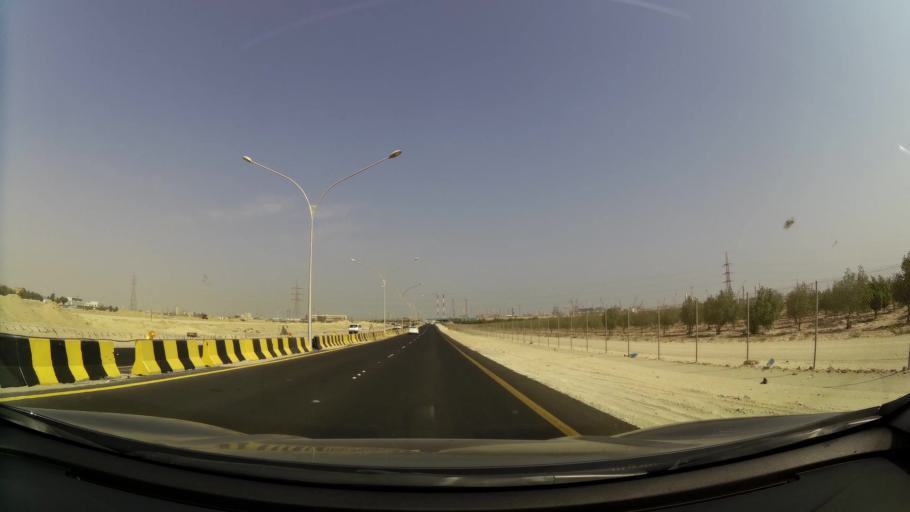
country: KW
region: Al Ahmadi
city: Al Fahahil
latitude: 28.9909
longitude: 48.1394
